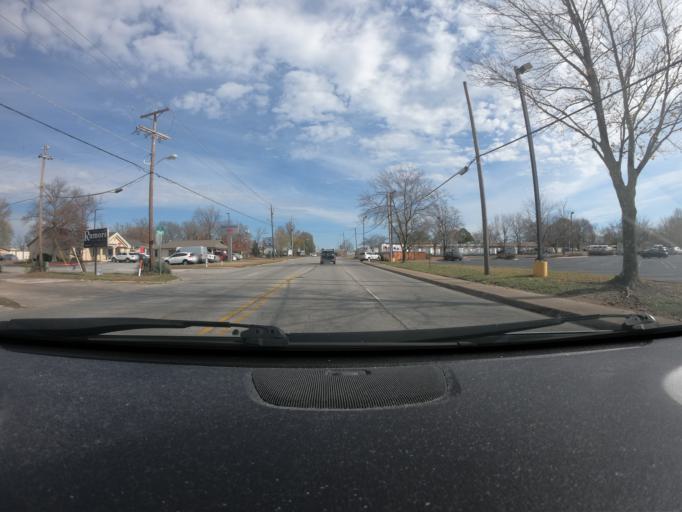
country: US
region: Arkansas
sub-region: Benton County
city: Rogers
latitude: 36.3338
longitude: -94.1333
